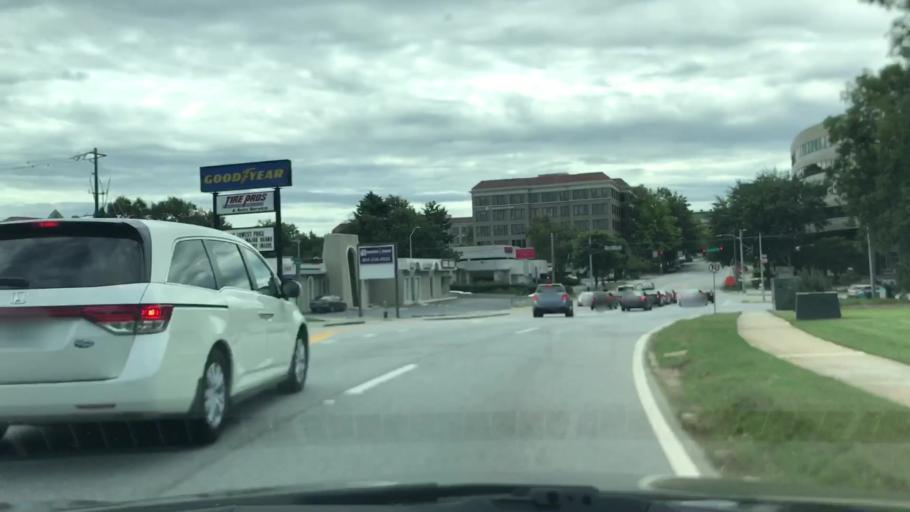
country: US
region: Georgia
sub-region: DeKalb County
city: Decatur
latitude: 33.7789
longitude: -84.2965
